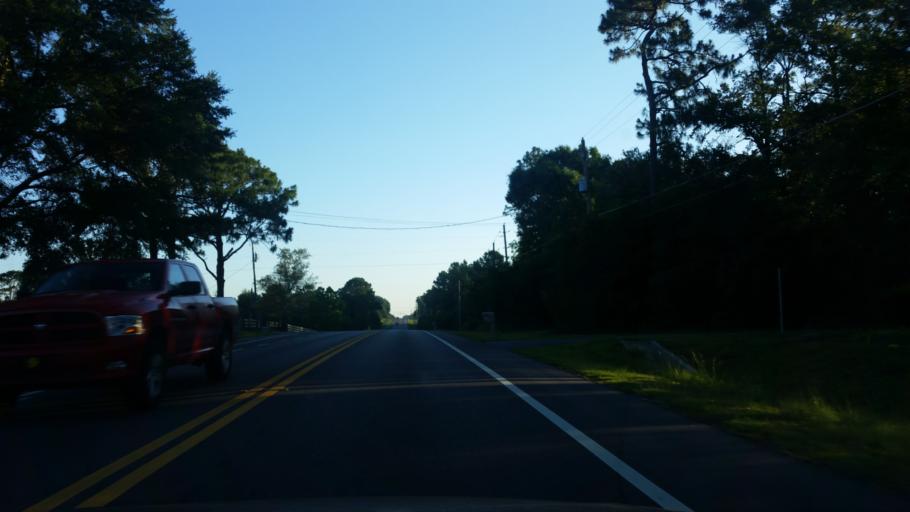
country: US
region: Florida
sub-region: Escambia County
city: Gonzalez
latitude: 30.5717
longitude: -87.3286
